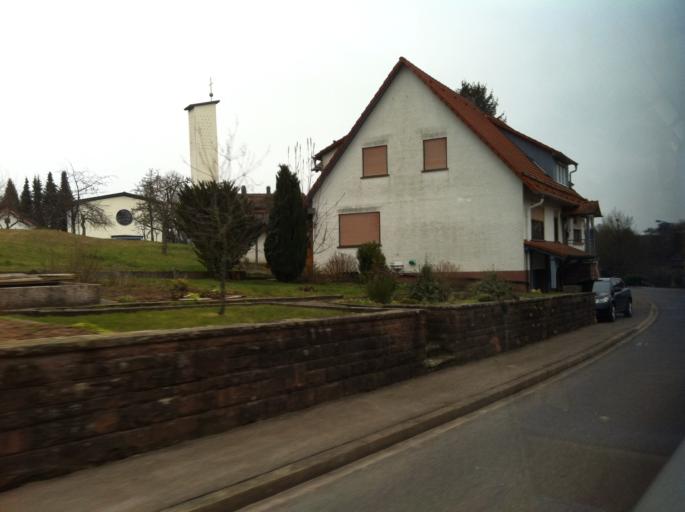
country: DE
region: Baden-Wuerttemberg
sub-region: Karlsruhe Region
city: Fahrenbach
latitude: 49.4403
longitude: 9.1633
